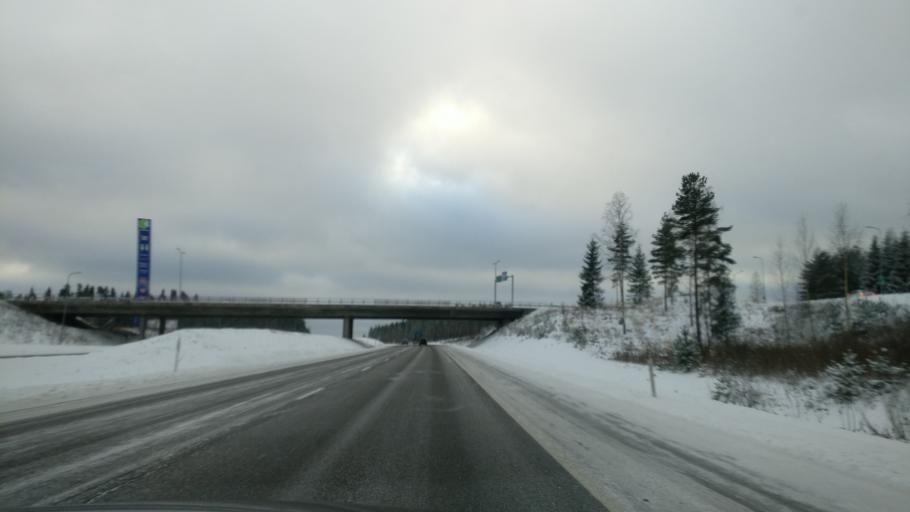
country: FI
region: Paijanne Tavastia
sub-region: Lahti
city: Heinola
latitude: 61.1143
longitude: 25.9248
